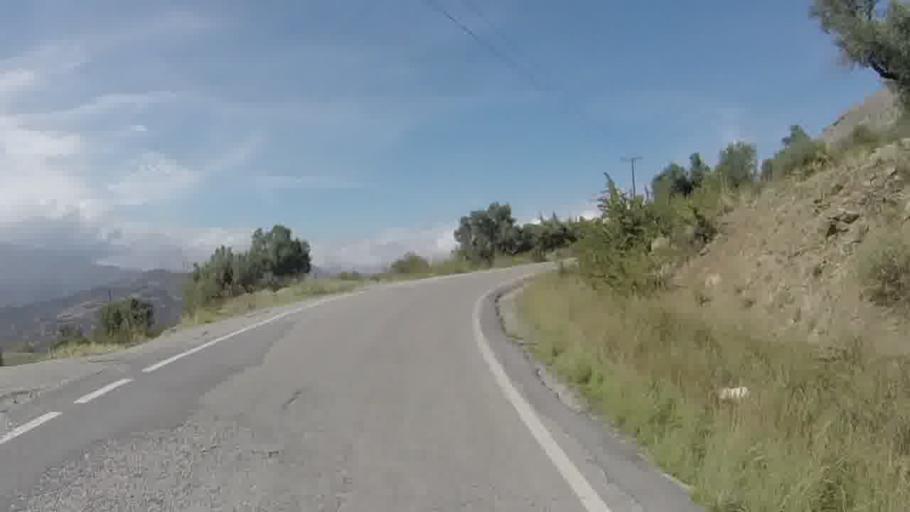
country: GR
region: Crete
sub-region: Nomos Rethymnis
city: Agia Galini
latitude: 35.1498
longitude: 24.7363
